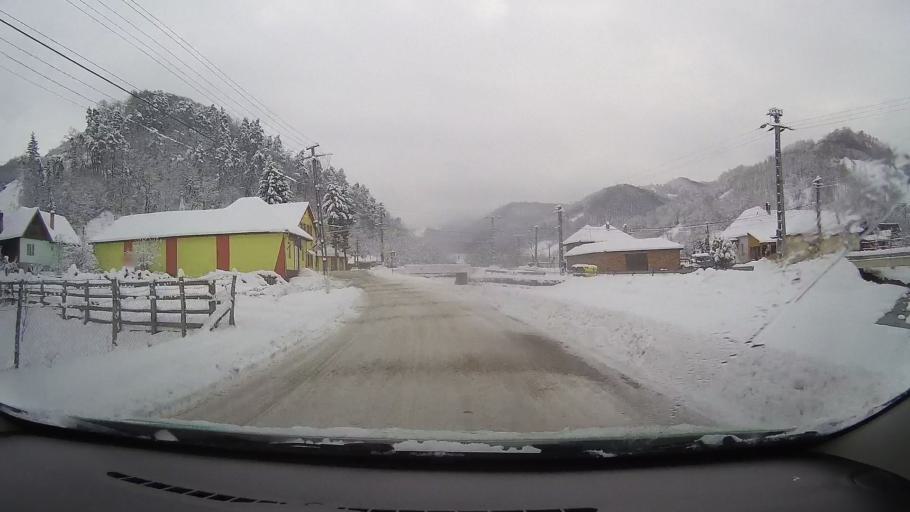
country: RO
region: Alba
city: Pianu de Sus
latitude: 45.8577
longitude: 23.5009
